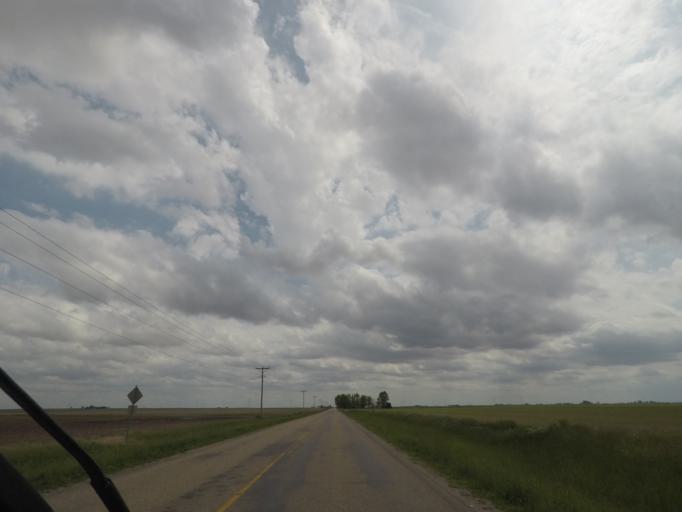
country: US
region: Illinois
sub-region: De Witt County
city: Clinton
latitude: 40.0908
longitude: -89.0859
